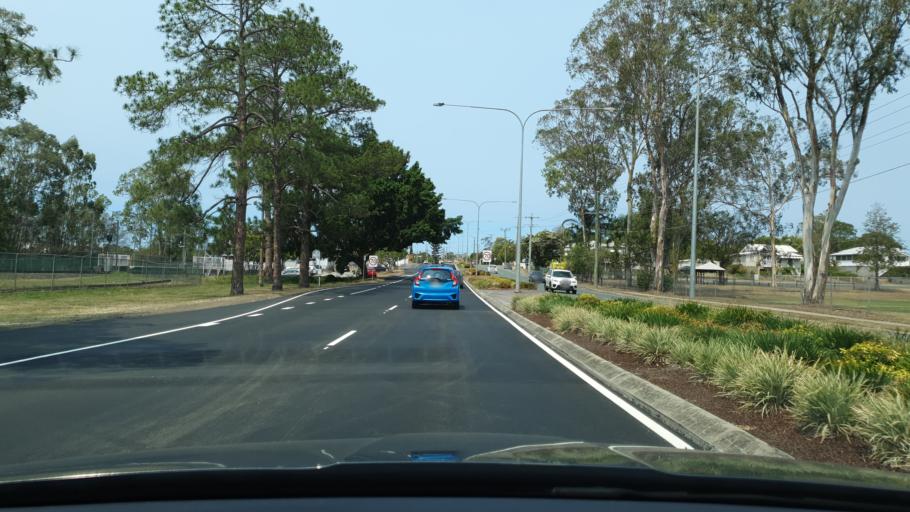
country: AU
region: Queensland
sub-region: Ipswich
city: Bundamba
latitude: -27.6043
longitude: 152.8207
